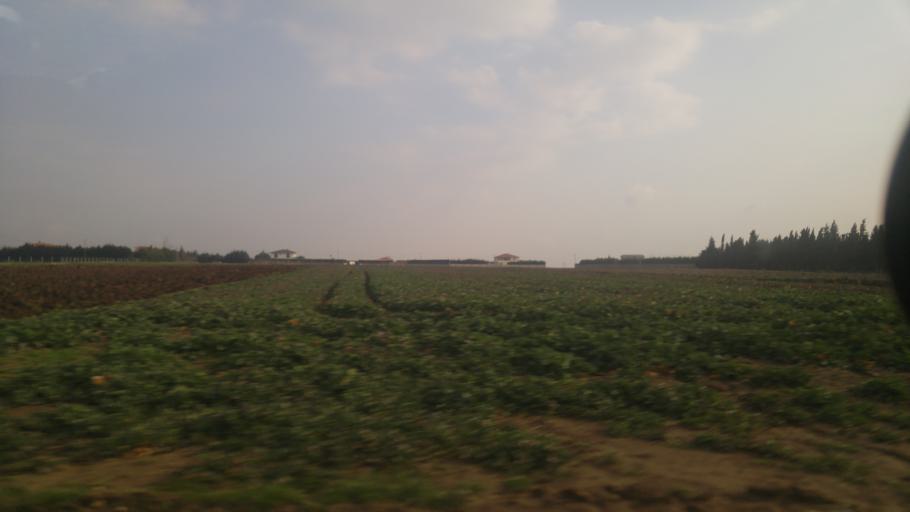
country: TR
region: Istanbul
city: Kavakli
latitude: 41.1170
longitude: 28.3082
